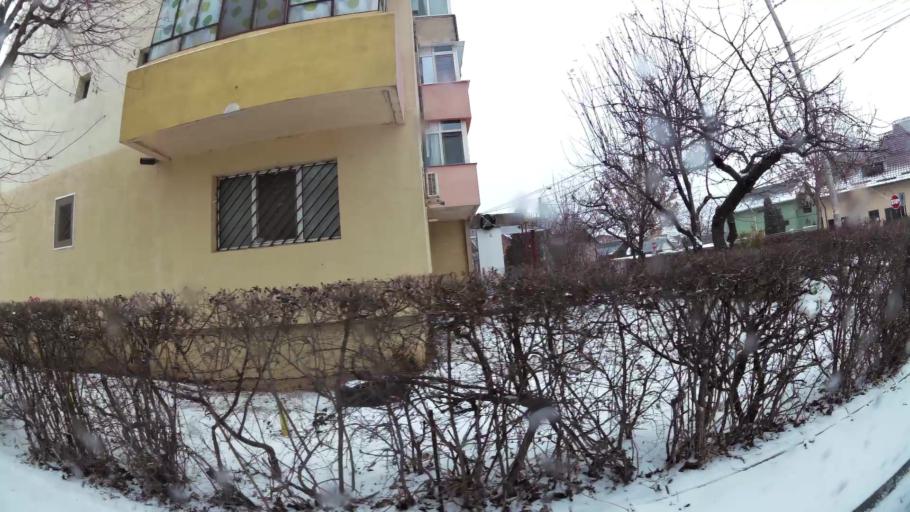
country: RO
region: Dambovita
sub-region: Municipiul Targoviste
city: Targoviste
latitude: 44.9325
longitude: 25.4407
